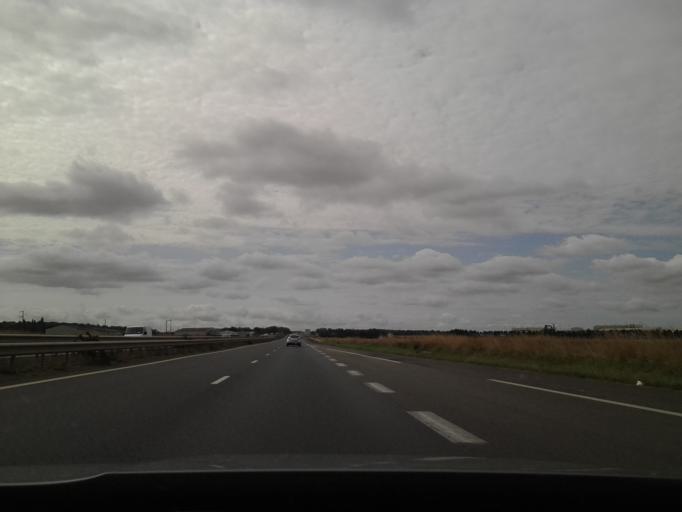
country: FR
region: Lower Normandy
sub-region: Departement du Calvados
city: Bourguebus
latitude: 49.0993
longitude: -0.3125
